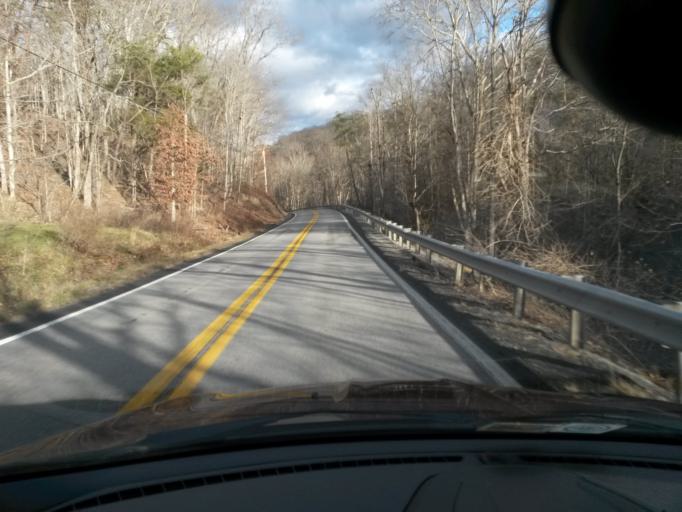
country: US
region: West Virginia
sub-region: Monroe County
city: Union
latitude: 37.4806
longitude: -80.6221
